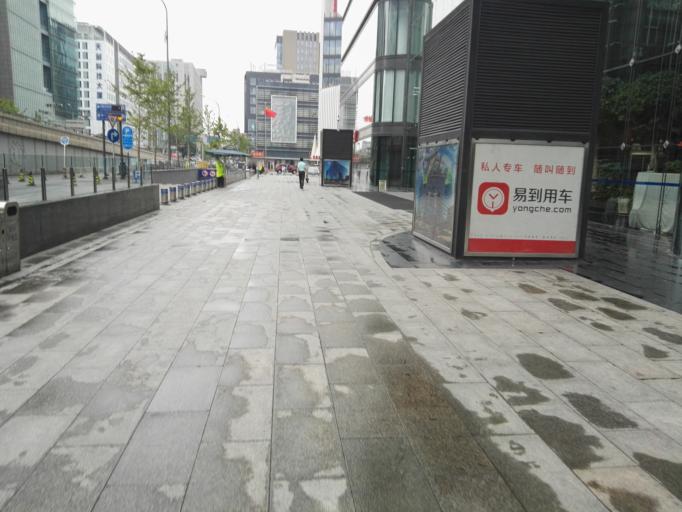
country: CN
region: Beijing
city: Haidian
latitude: 39.9829
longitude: 116.3018
